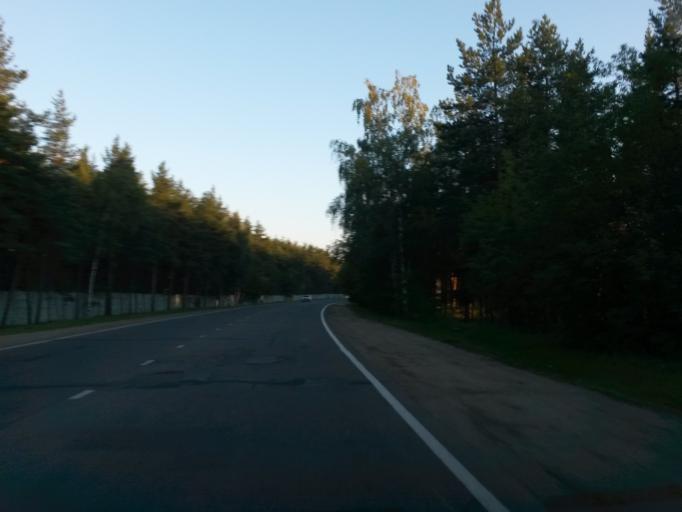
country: RU
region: Jaroslavl
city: Yaroslavl
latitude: 57.6736
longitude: 39.9078
